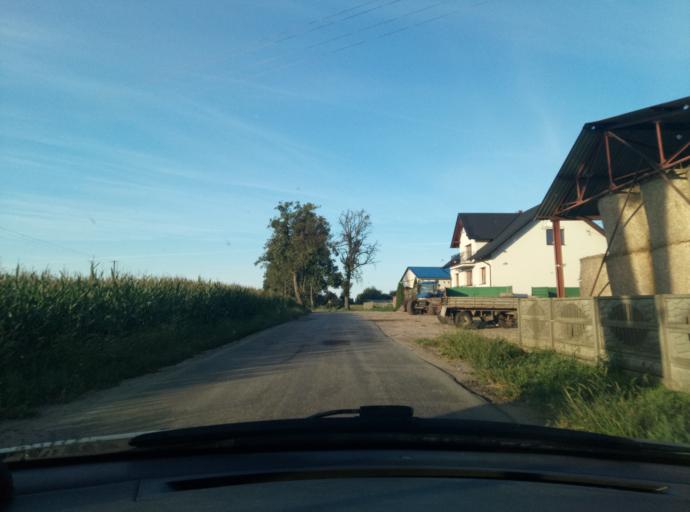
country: PL
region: Kujawsko-Pomorskie
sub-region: Powiat brodnicki
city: Jablonowo Pomorskie
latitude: 53.4189
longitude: 19.1813
